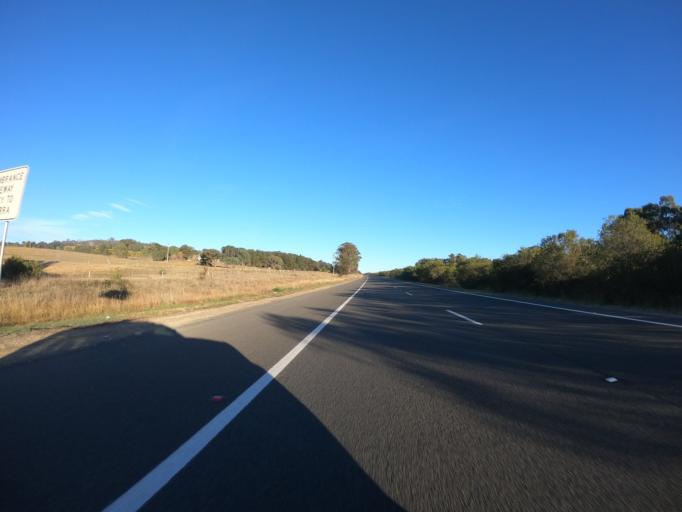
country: AU
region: New South Wales
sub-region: Yass Valley
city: Gundaroo
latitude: -35.1812
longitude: 149.2484
